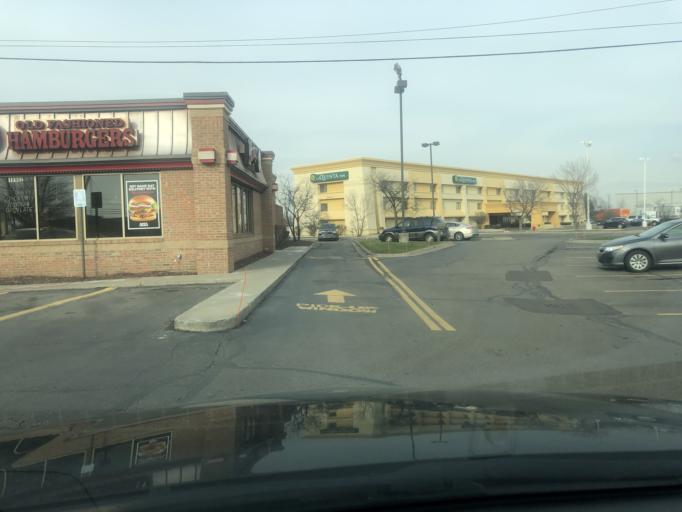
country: US
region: Michigan
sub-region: Wayne County
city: Southgate
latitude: 42.2135
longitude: -83.2264
